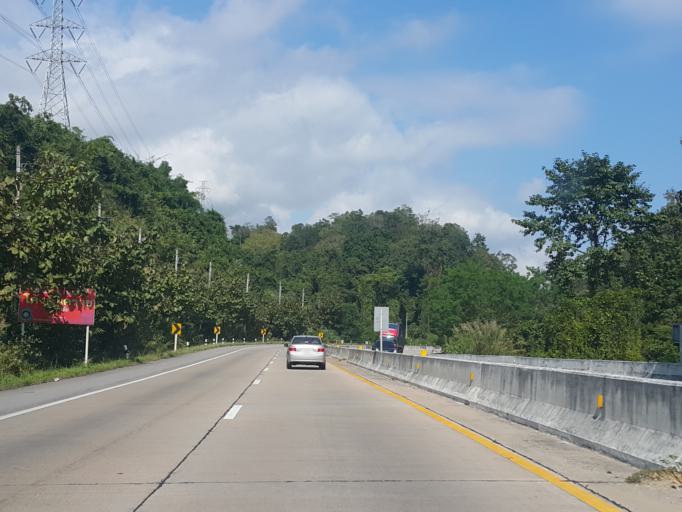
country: TH
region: Lamphun
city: Mae Tha
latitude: 18.3972
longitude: 99.2150
